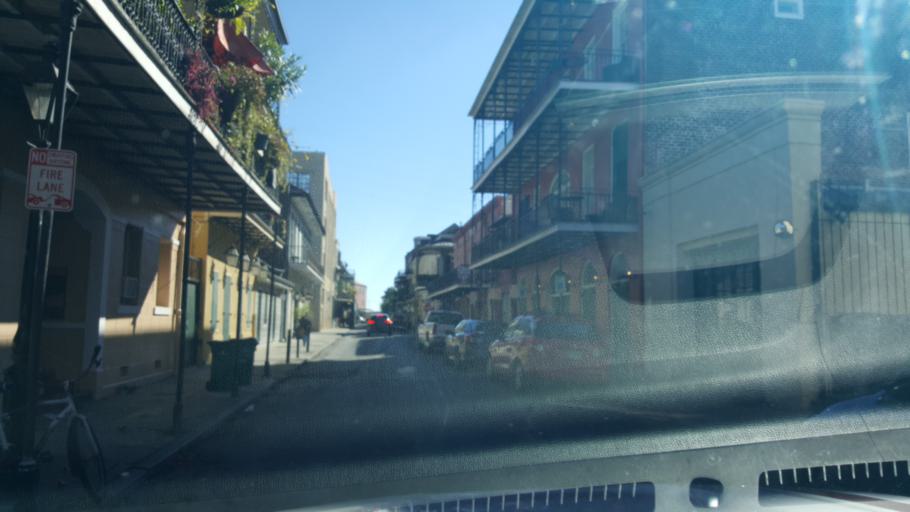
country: US
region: Louisiana
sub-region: Orleans Parish
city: New Orleans
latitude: 29.9602
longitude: -90.0623
